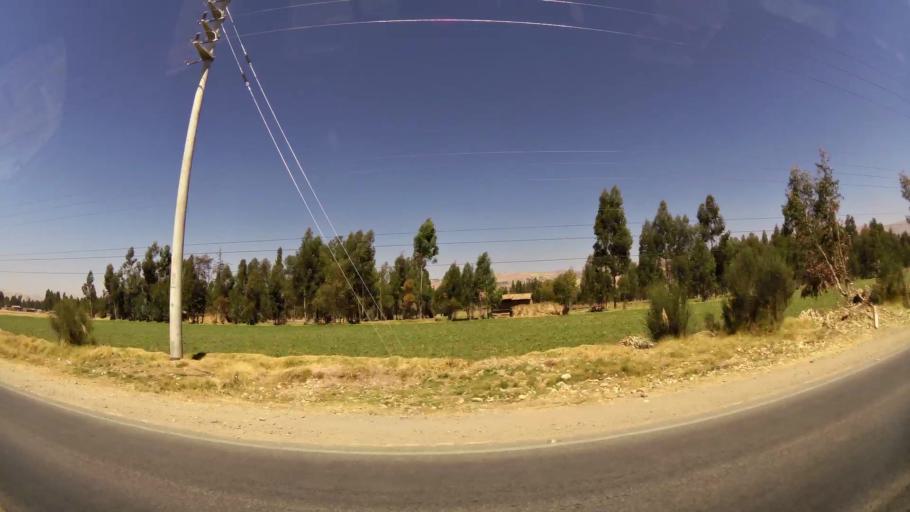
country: PE
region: Junin
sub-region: Provincia de Jauja
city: Apata
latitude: -11.8730
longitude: -75.3665
